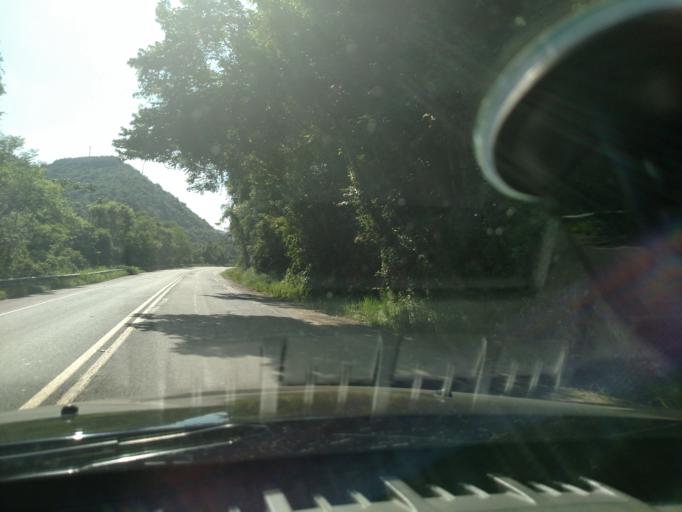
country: BR
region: Santa Catarina
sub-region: Ibirama
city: Ibirama
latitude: -27.0864
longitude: -49.4780
